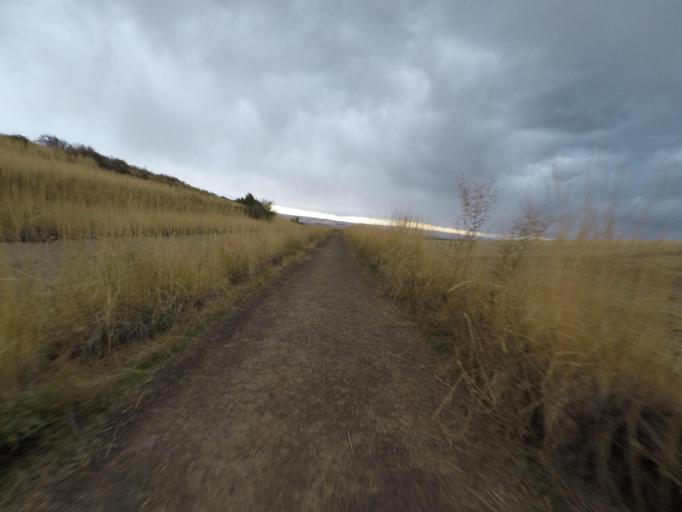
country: US
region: Washington
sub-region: Walla Walla County
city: Walla Walla East
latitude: 46.0663
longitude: -118.2684
